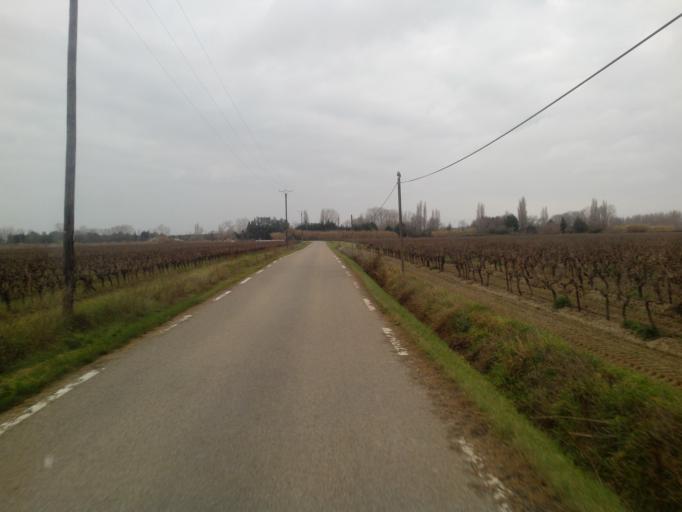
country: FR
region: Languedoc-Roussillon
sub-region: Departement du Gard
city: Saint-Gilles
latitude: 43.5837
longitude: 4.3439
